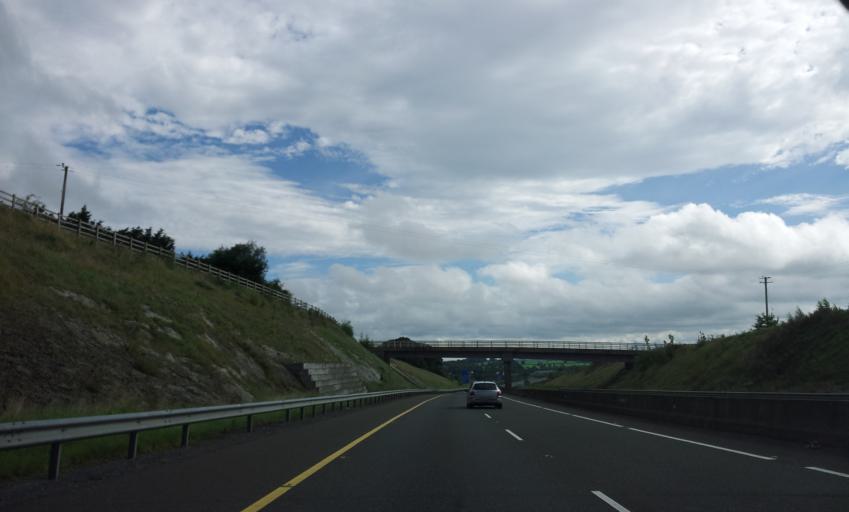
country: IE
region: Munster
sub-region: North Tipperary
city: Nenagh
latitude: 52.8420
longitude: -8.2743
